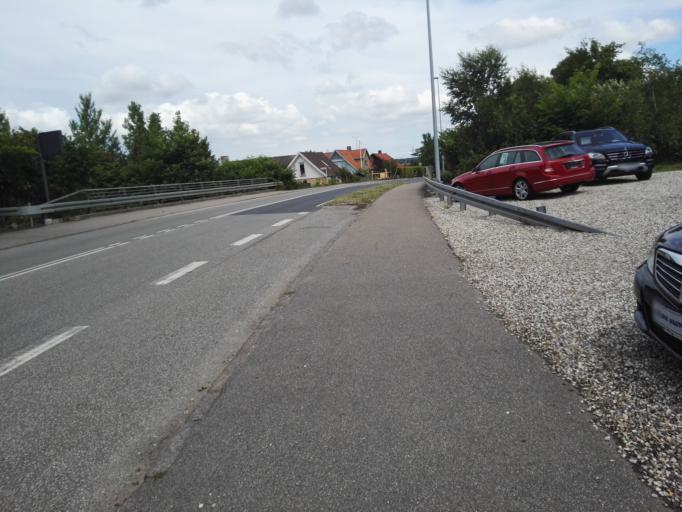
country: DK
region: Capital Region
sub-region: Frederikssund Kommune
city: Slangerup
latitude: 55.8868
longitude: 12.1981
